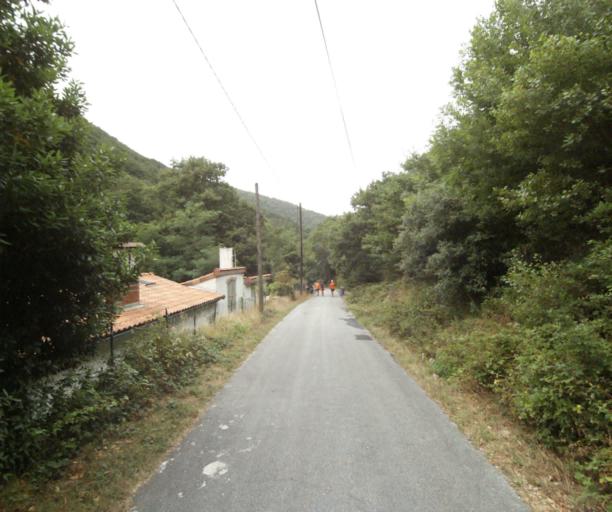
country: FR
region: Midi-Pyrenees
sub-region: Departement du Tarn
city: Soreze
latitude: 43.4293
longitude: 2.0788
